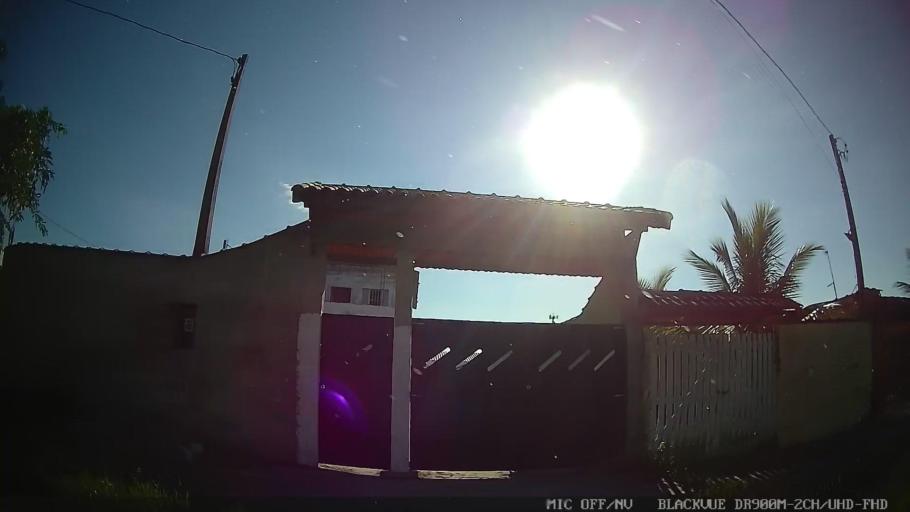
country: BR
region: Sao Paulo
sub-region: Itanhaem
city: Itanhaem
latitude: -24.2251
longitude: -46.8810
